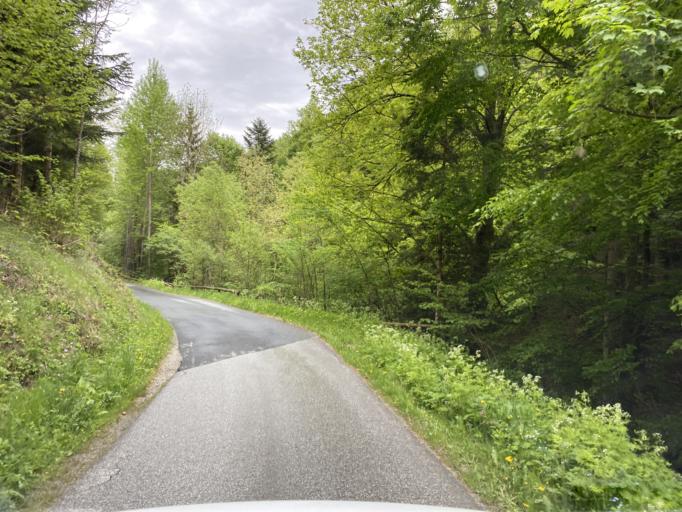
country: AT
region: Styria
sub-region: Politischer Bezirk Weiz
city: Koglhof
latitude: 47.3327
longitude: 15.6639
